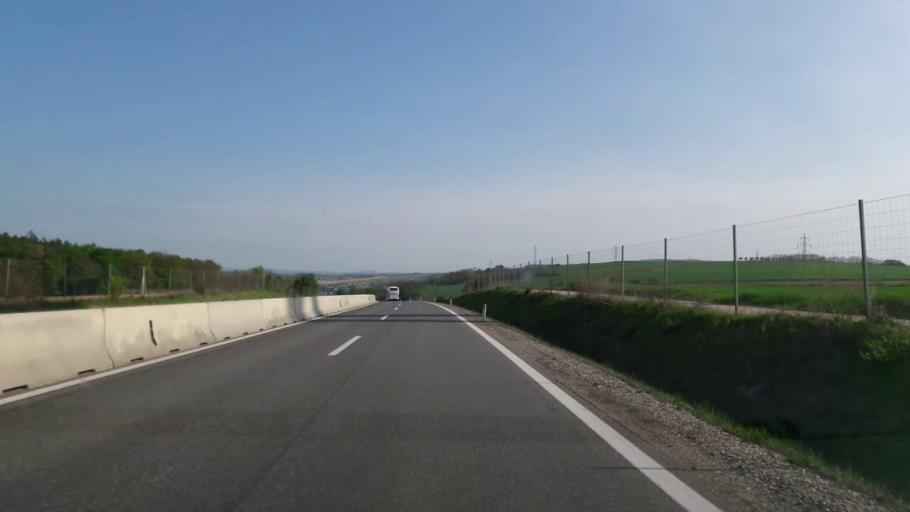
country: AT
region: Lower Austria
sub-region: Politischer Bezirk Hollabrunn
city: Hollabrunn
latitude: 48.5298
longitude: 16.0815
